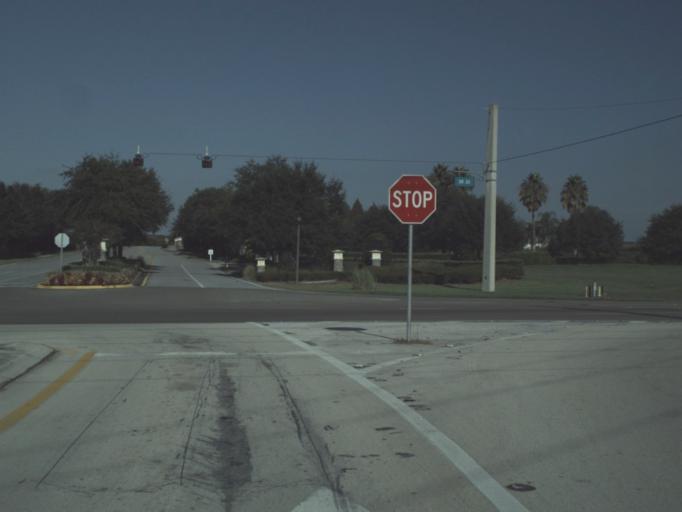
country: US
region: Florida
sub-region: Polk County
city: Combee Settlement
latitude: 28.1178
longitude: -81.9079
